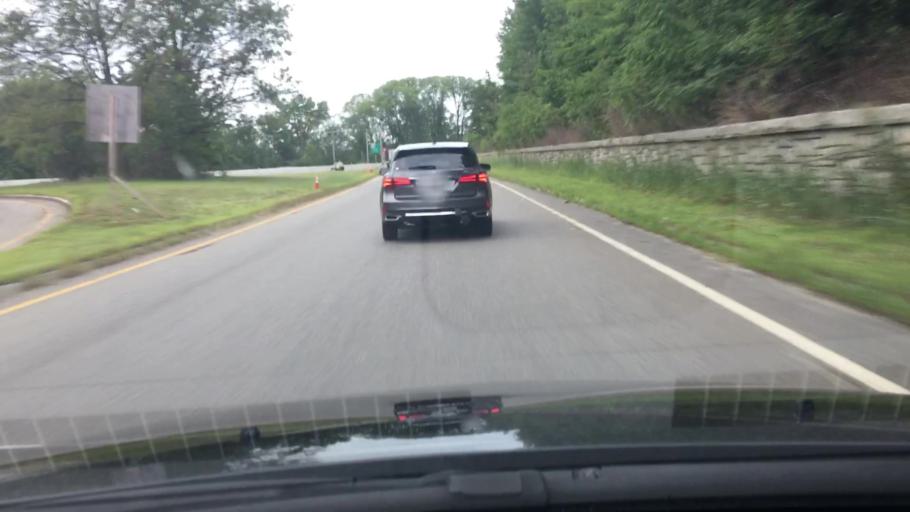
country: US
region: Massachusetts
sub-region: Worcester County
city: Shrewsbury
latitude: 42.2821
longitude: -71.6693
